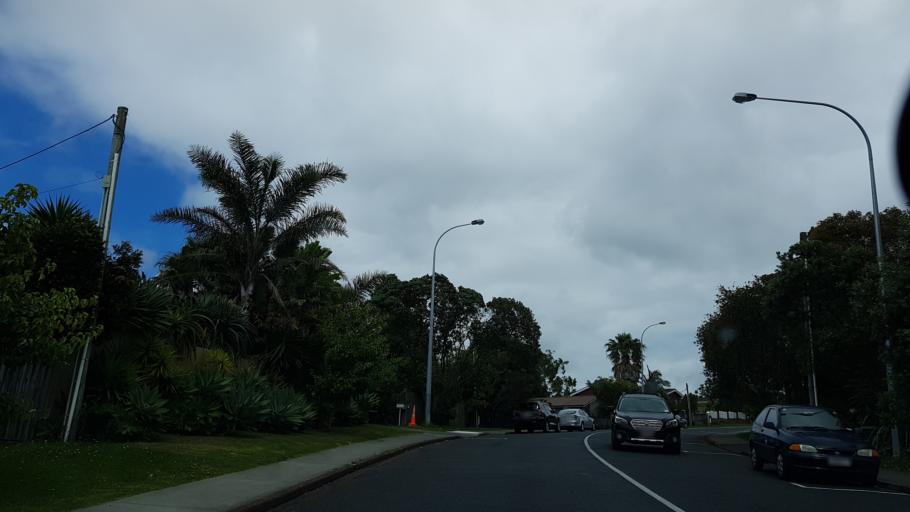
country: NZ
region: Auckland
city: Murrays Bay
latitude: -36.7357
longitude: 174.7472
